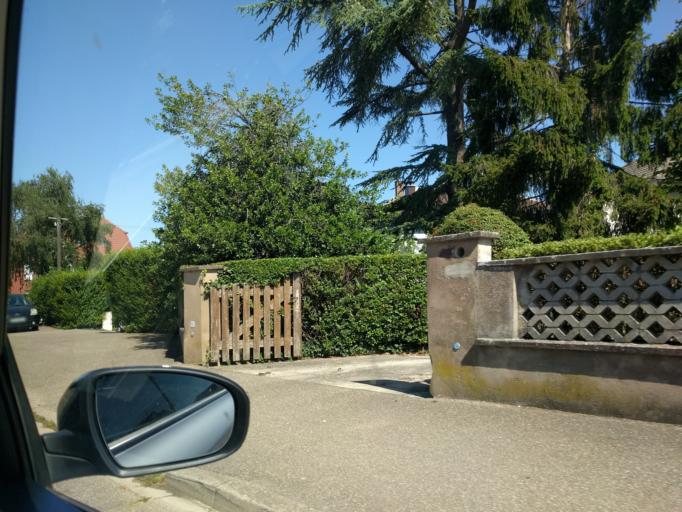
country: FR
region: Alsace
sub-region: Departement du Bas-Rhin
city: Geispolsheim
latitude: 48.5181
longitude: 7.6486
